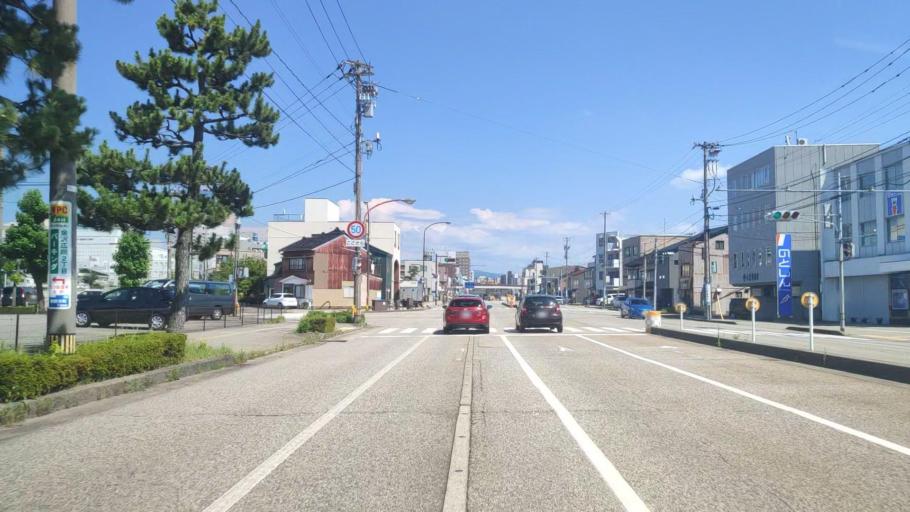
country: JP
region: Ishikawa
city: Kanazawa-shi
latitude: 36.5778
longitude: 136.6400
